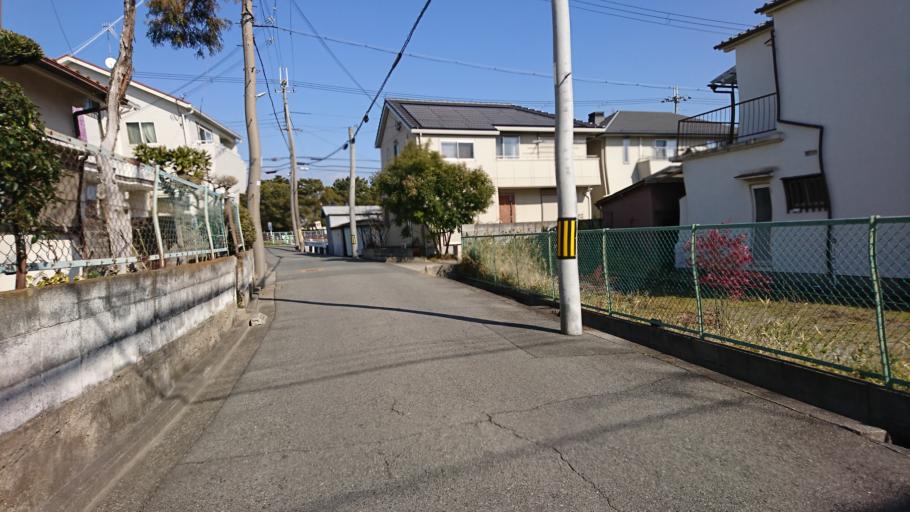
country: JP
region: Hyogo
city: Kakogawacho-honmachi
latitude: 34.7382
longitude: 134.8672
